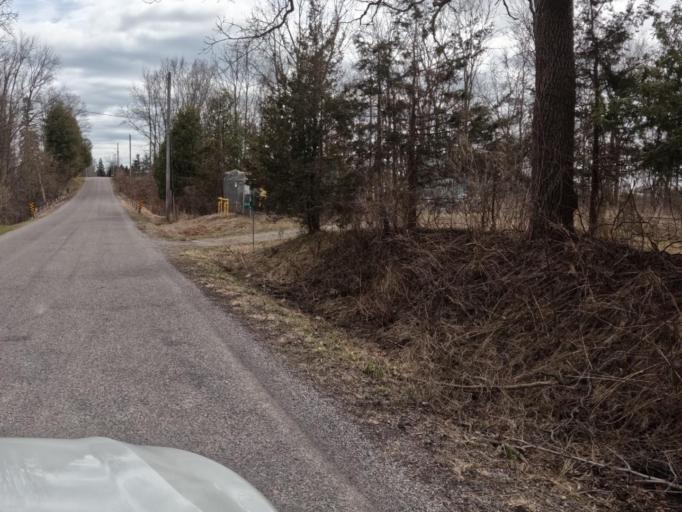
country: CA
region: Ontario
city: Norfolk County
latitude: 42.8053
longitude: -80.2152
